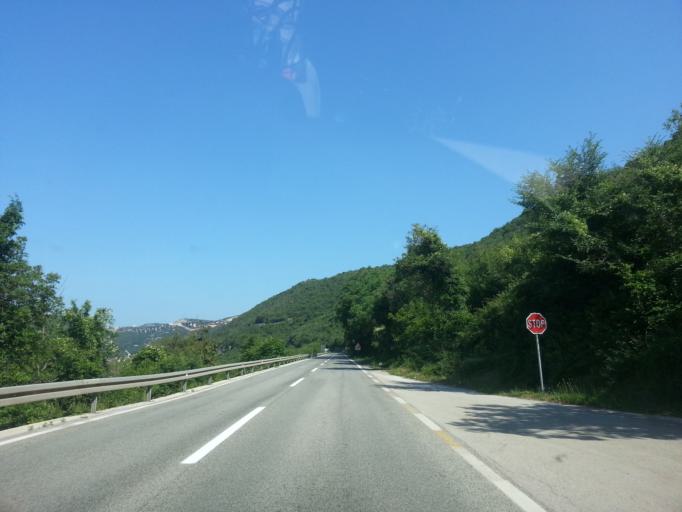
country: HR
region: Primorsko-Goranska
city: Krasica
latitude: 45.2951
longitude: 14.5642
